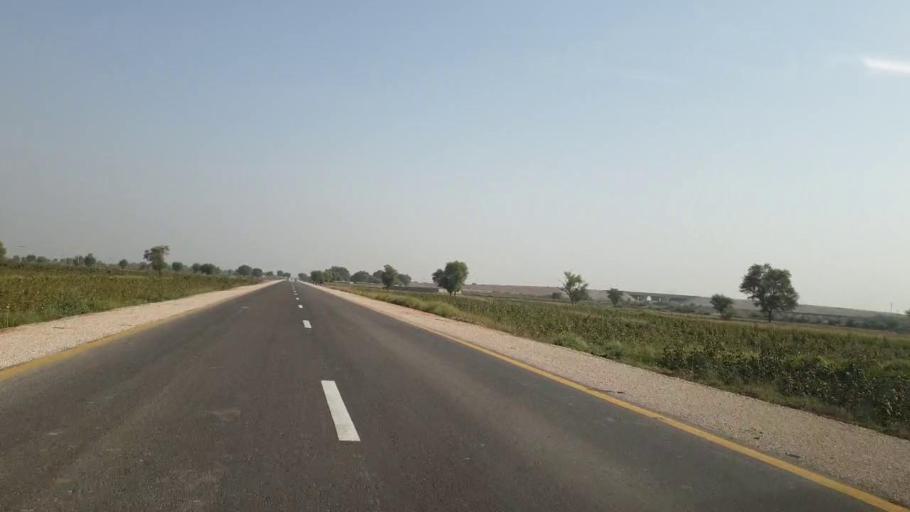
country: PK
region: Sindh
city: Sehwan
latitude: 26.4612
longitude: 67.8021
